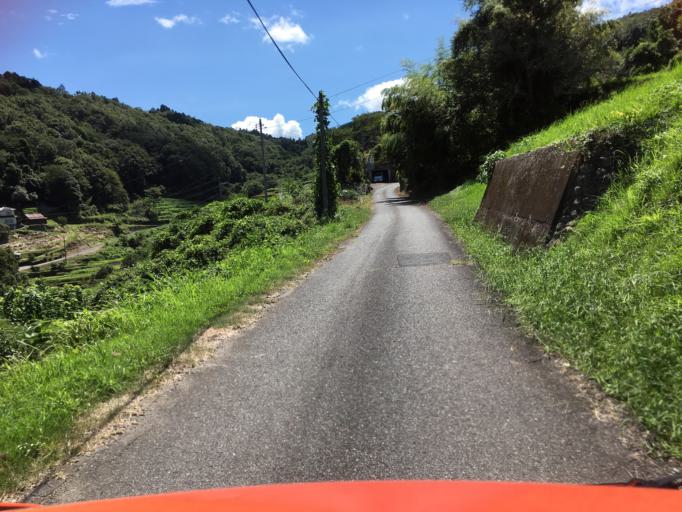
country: JP
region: Okayama
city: Tsuyama
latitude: 34.8989
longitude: 134.1358
